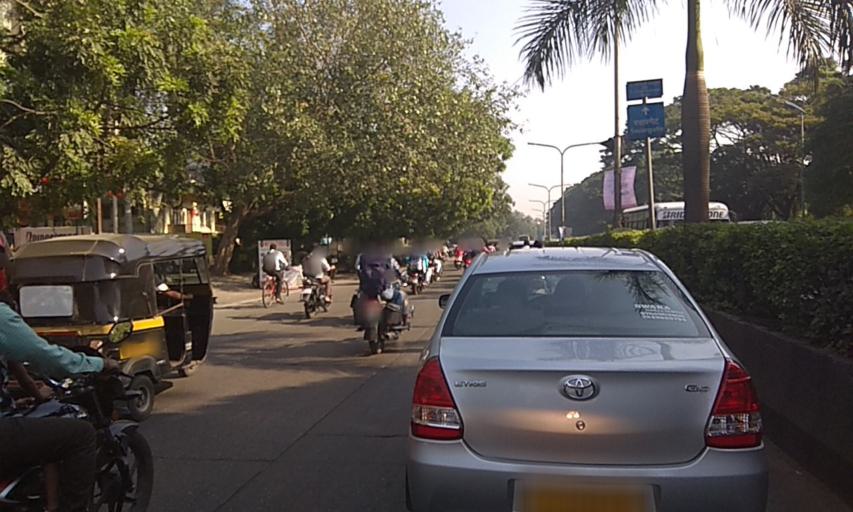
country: IN
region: Maharashtra
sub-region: Pune Division
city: Pune
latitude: 18.4965
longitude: 73.8388
